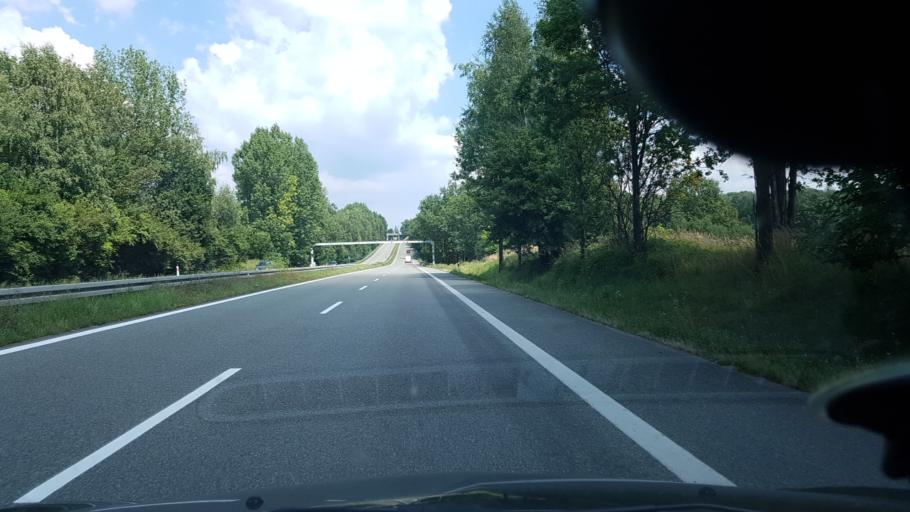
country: PL
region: Silesian Voivodeship
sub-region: Powiat mikolowski
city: Laziska Gorne
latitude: 50.1429
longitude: 18.8438
